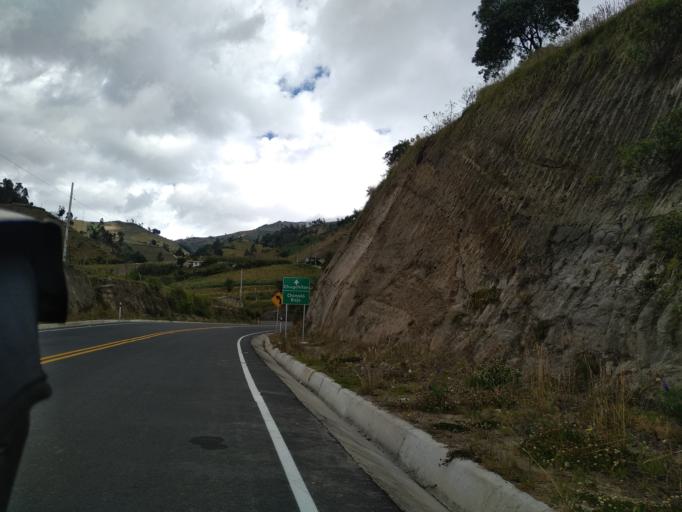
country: EC
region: Cotopaxi
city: Saquisili
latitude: -0.7727
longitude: -78.9091
